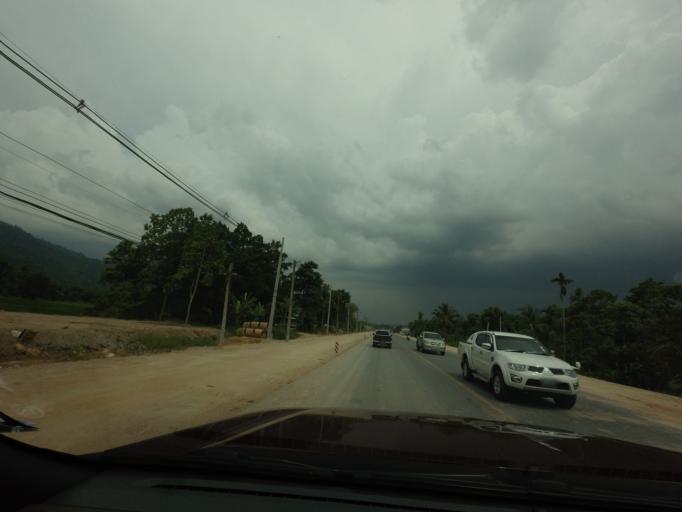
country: TH
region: Yala
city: Krong Pi Nang
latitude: 6.4492
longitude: 101.2760
